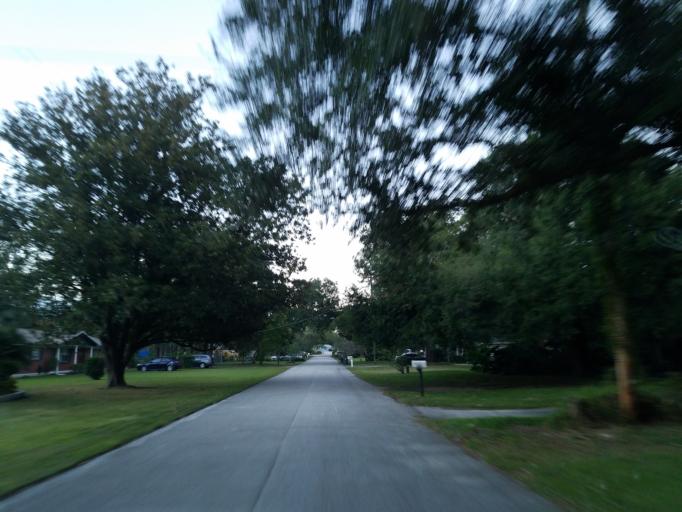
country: US
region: Florida
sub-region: Hillsborough County
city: Brandon
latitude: 27.9214
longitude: -82.2633
